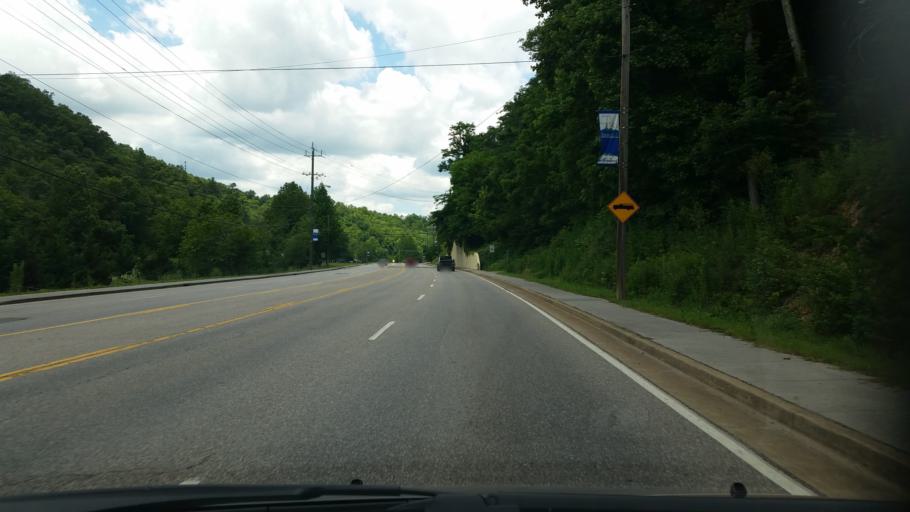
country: US
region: Tennessee
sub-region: Sevier County
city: Gatlinburg
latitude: 35.7266
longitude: -83.4755
